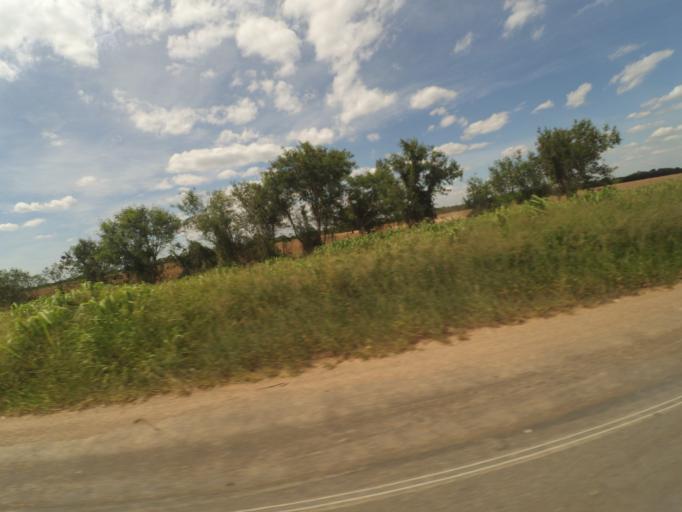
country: BO
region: Santa Cruz
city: Pailon
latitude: -17.5854
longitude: -62.0535
